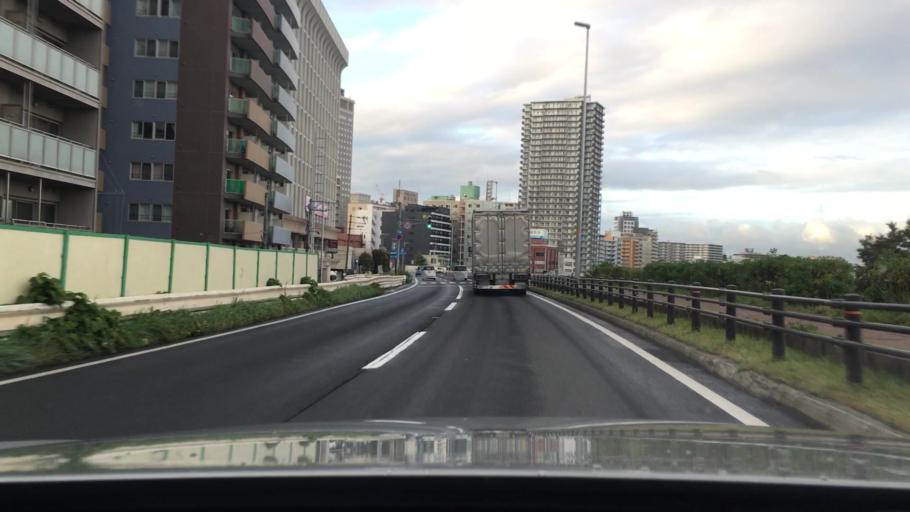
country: JP
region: Hokkaido
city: Sapporo
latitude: 43.0455
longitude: 141.3582
